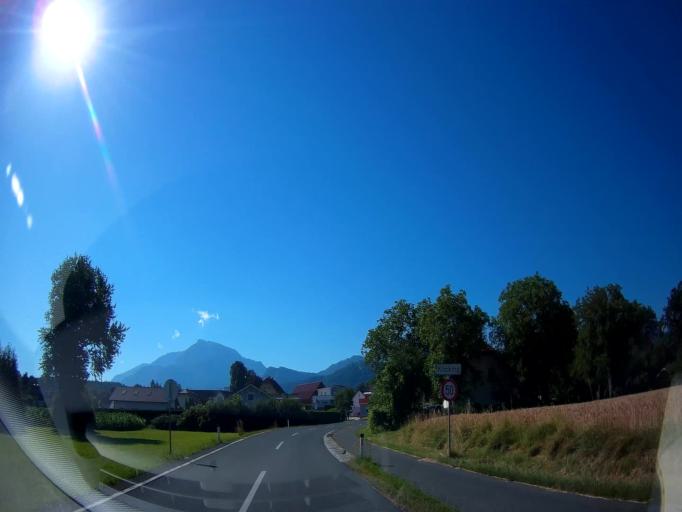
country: AT
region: Carinthia
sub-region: Politischer Bezirk Volkermarkt
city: Eberndorf
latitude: 46.5799
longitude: 14.6530
